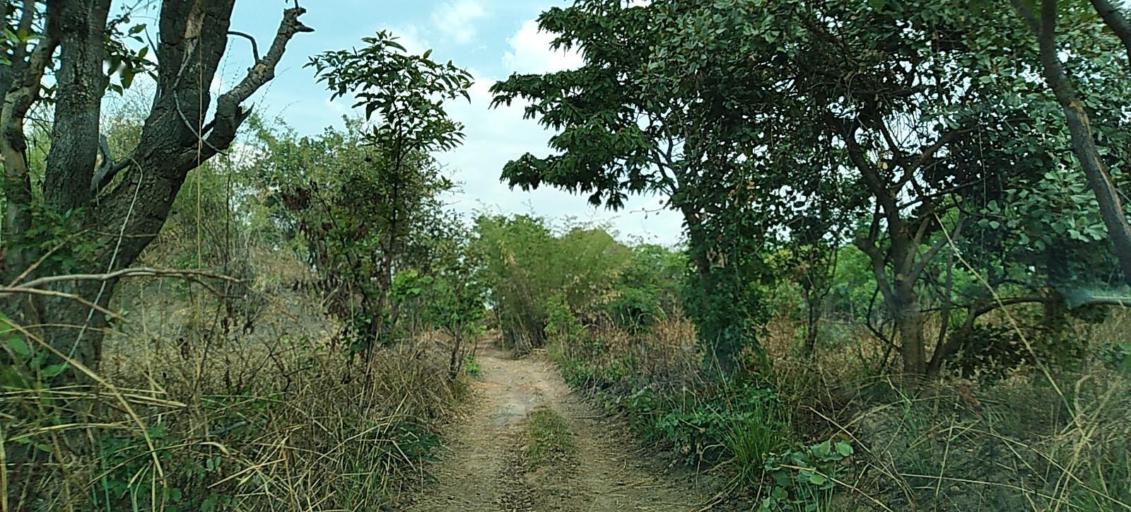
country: ZM
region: Copperbelt
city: Chililabombwe
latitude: -12.3405
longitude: 27.7832
